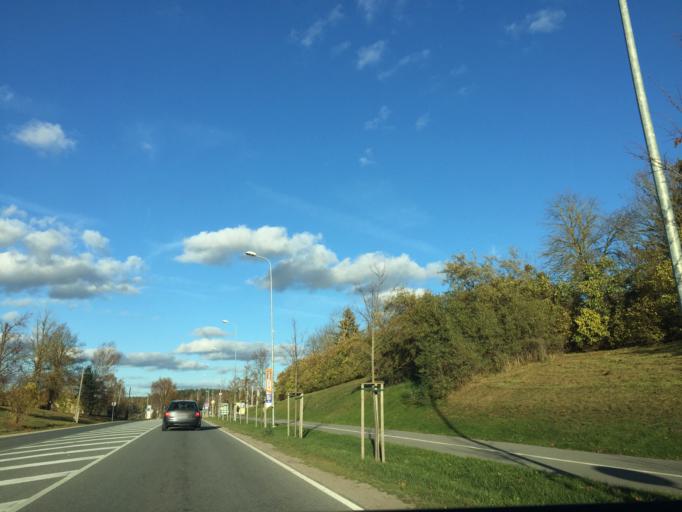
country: LV
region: Tukuma Rajons
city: Tukums
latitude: 56.9530
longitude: 23.1175
